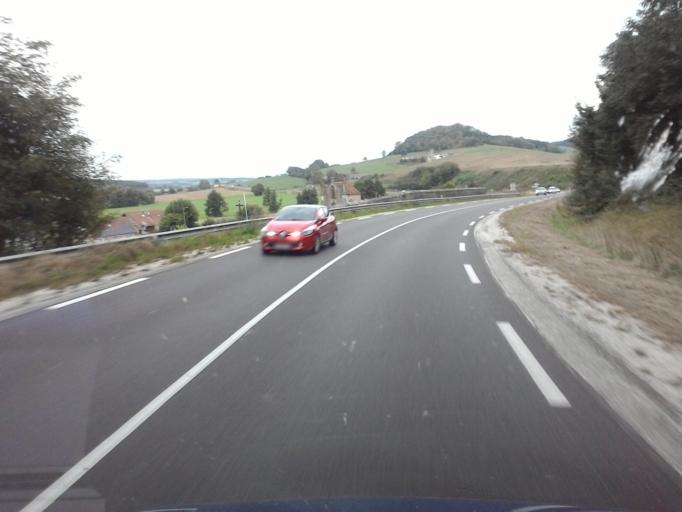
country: FR
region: Franche-Comte
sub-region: Departement de la Haute-Saone
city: Frotey-les-Vesoul
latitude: 47.6624
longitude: 6.2155
